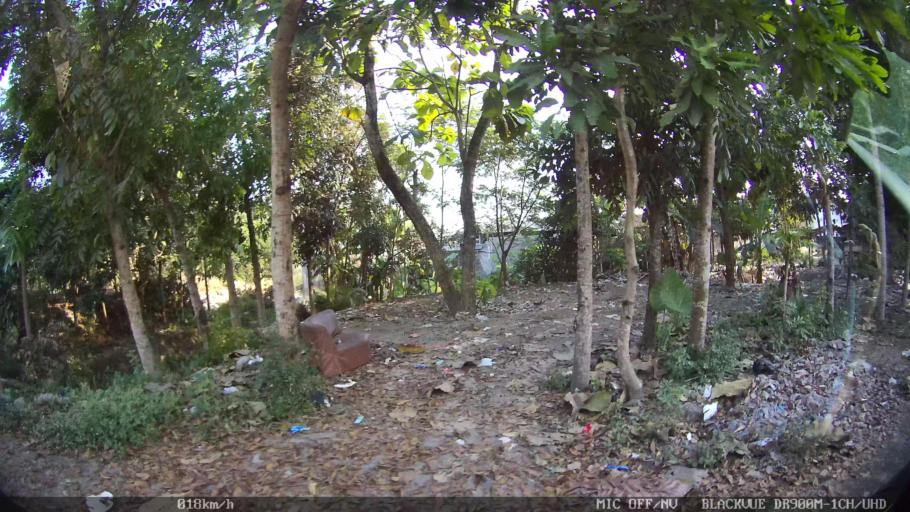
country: ID
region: Daerah Istimewa Yogyakarta
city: Gamping Lor
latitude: -7.7949
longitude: 110.3344
